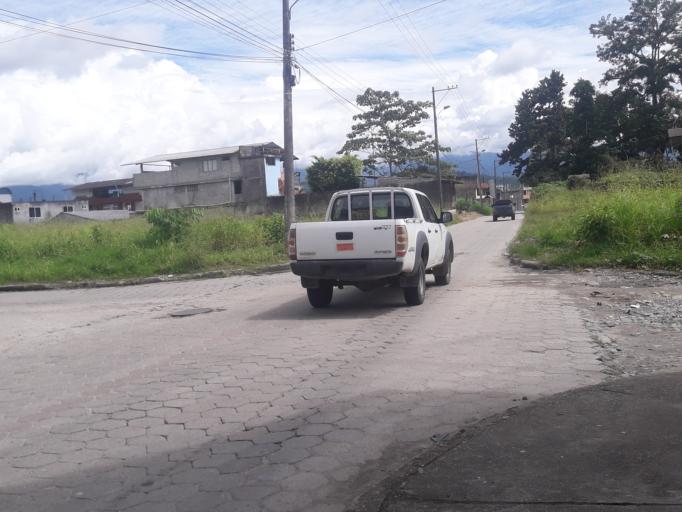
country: EC
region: Napo
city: Tena
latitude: -1.0043
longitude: -77.8098
